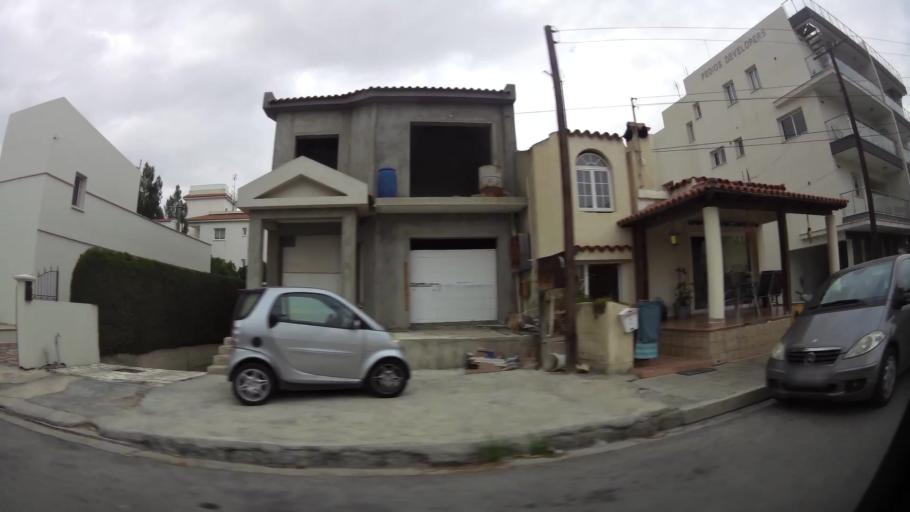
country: CY
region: Lefkosia
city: Geri
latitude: 35.1148
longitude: 33.3793
